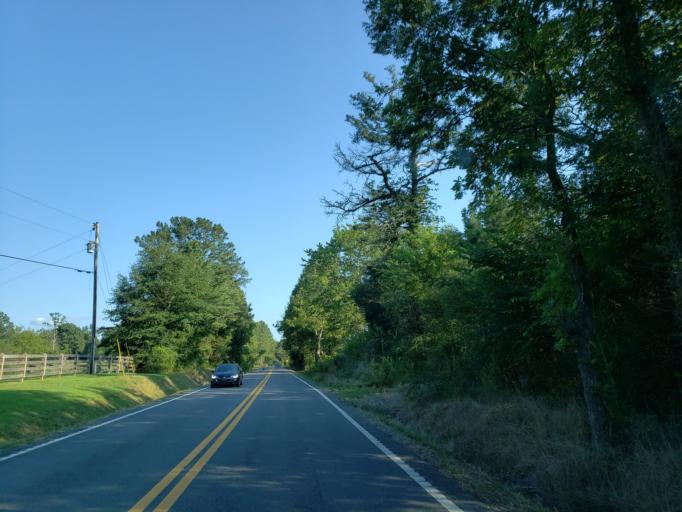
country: US
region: Tennessee
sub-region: Bradley County
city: Wildwood Lake
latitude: 35.0000
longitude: -84.7772
